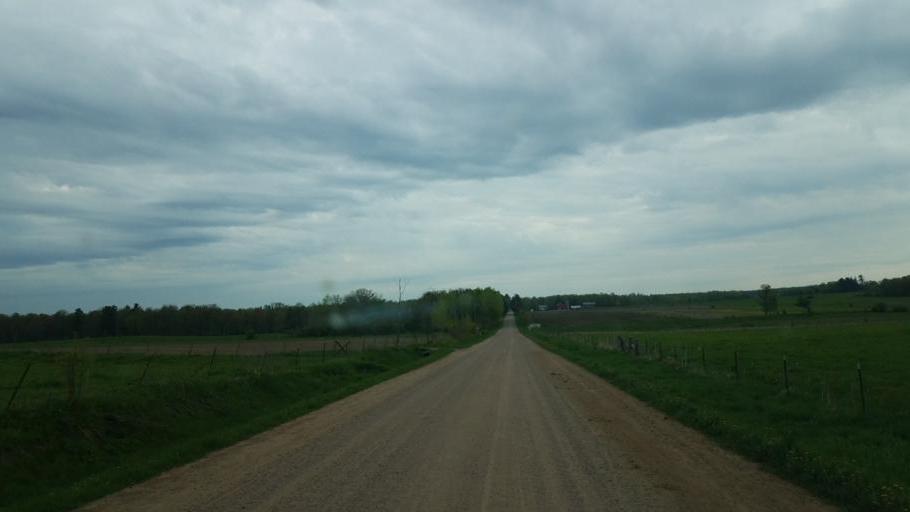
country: US
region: Wisconsin
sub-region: Marathon County
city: Spencer
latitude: 44.6006
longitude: -90.3764
